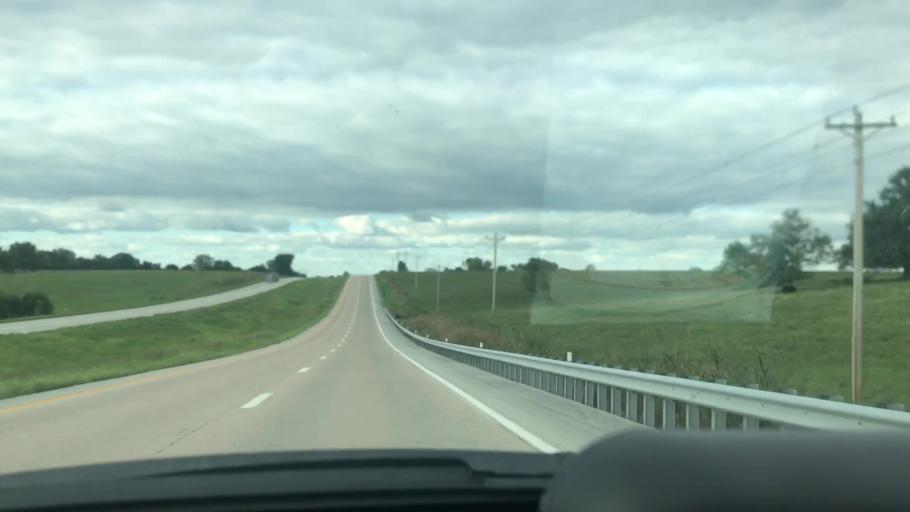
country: US
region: Missouri
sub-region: Benton County
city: Lincoln
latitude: 38.3241
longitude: -93.3419
